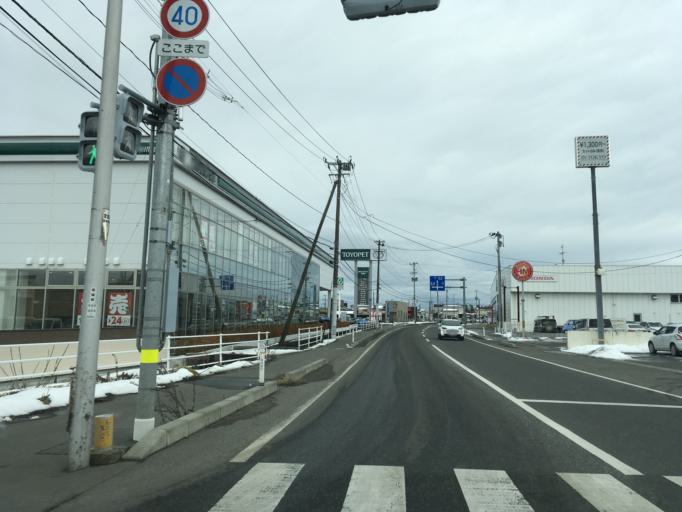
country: JP
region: Miyagi
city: Furukawa
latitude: 38.5699
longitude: 140.9590
